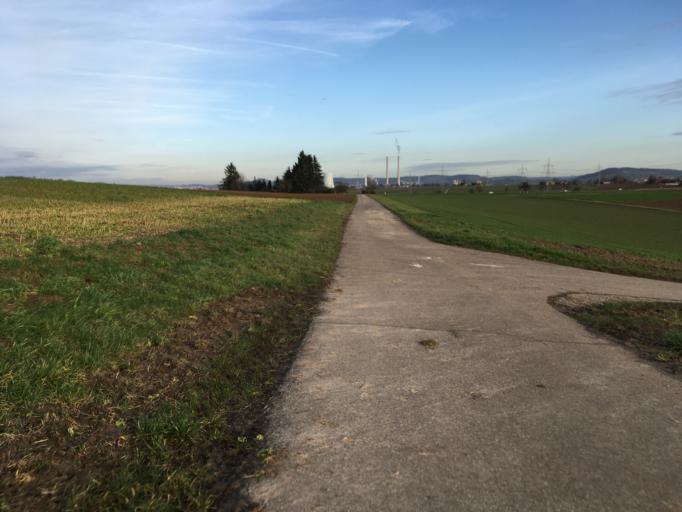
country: DE
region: Baden-Wuerttemberg
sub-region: Regierungsbezirk Stuttgart
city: Leingarten
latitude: 49.1687
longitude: 9.1520
